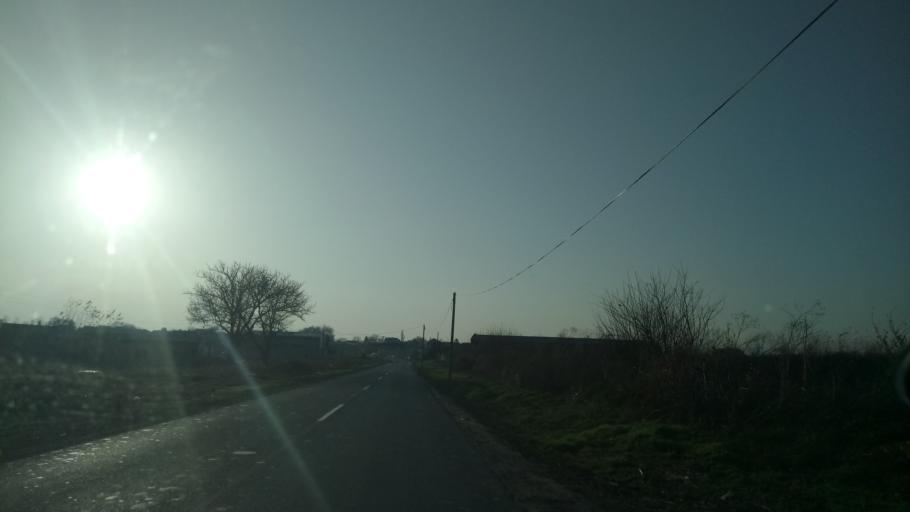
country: RS
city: Beska
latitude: 45.1319
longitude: 20.0837
